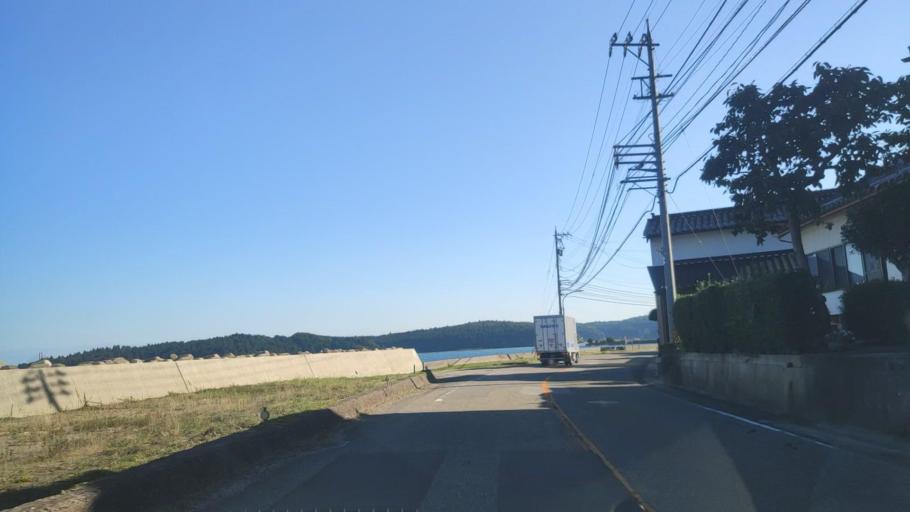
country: JP
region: Ishikawa
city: Nanao
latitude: 37.1525
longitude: 136.8794
